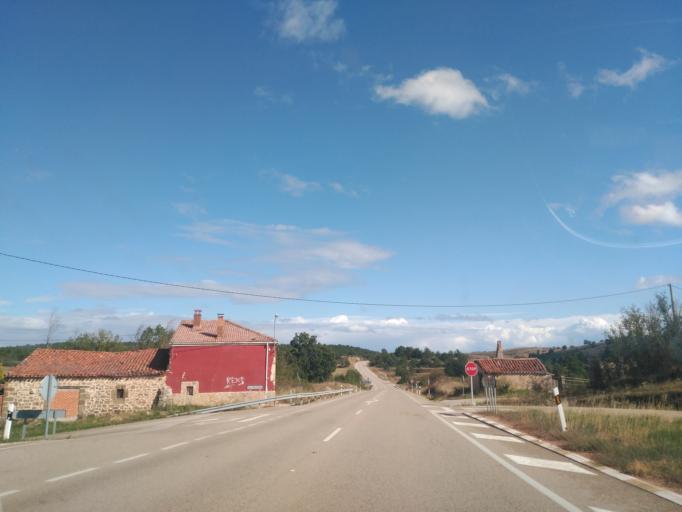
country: ES
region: Castille and Leon
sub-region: Provincia de Burgos
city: Cabezon de la Sierra
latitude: 41.8967
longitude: -3.2645
